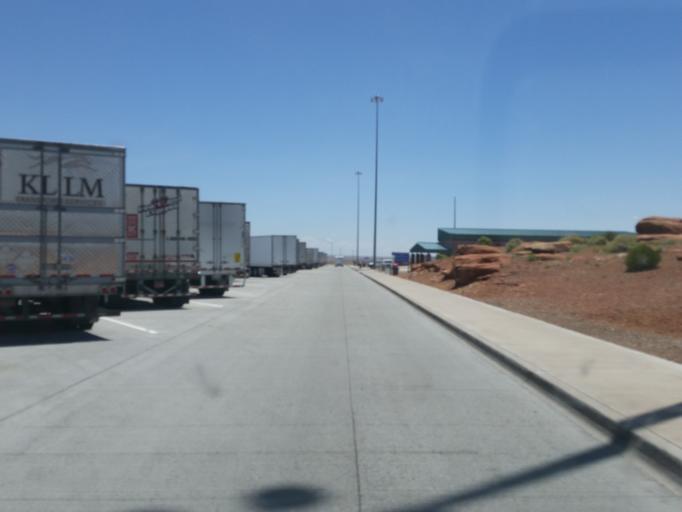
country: US
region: Arizona
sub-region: Coconino County
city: LeChee
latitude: 35.1052
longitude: -111.0057
